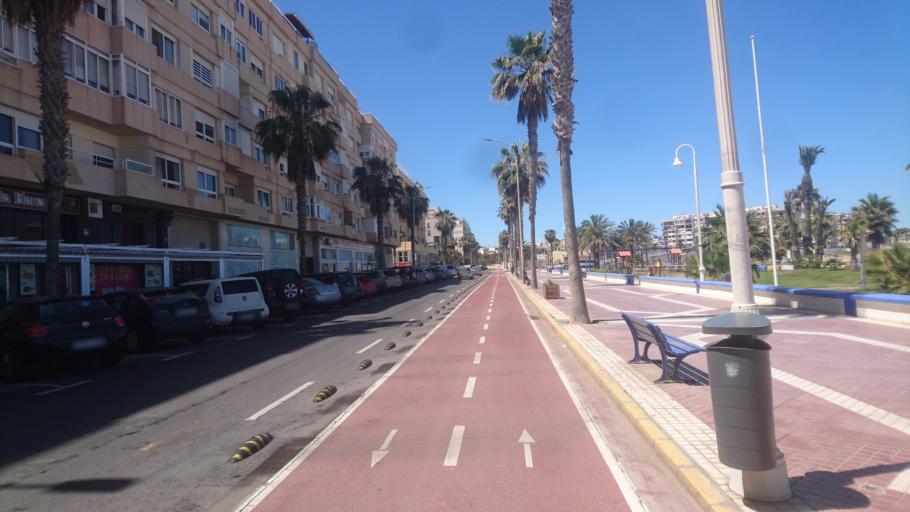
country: ES
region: Melilla
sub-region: Melilla
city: Melilla
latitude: 35.2835
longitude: -2.9384
